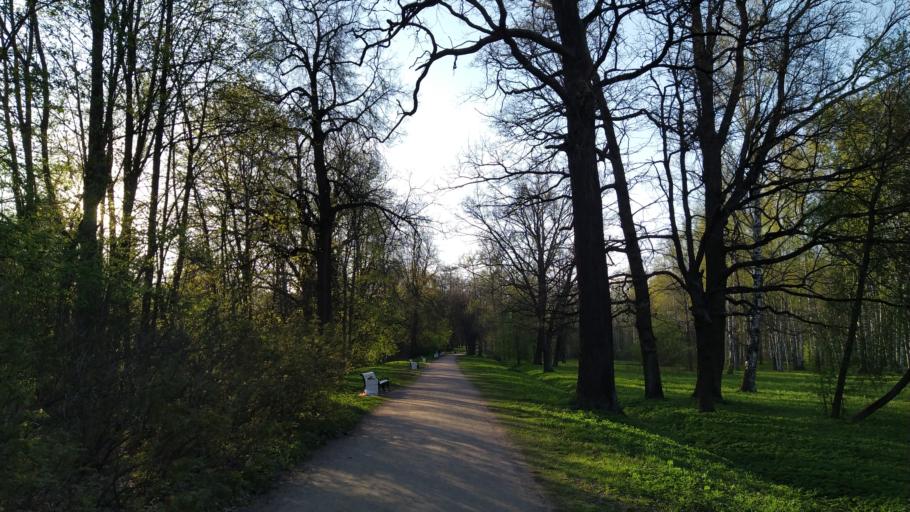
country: RU
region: St.-Petersburg
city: Pavlovsk
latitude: 59.6984
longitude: 30.4279
